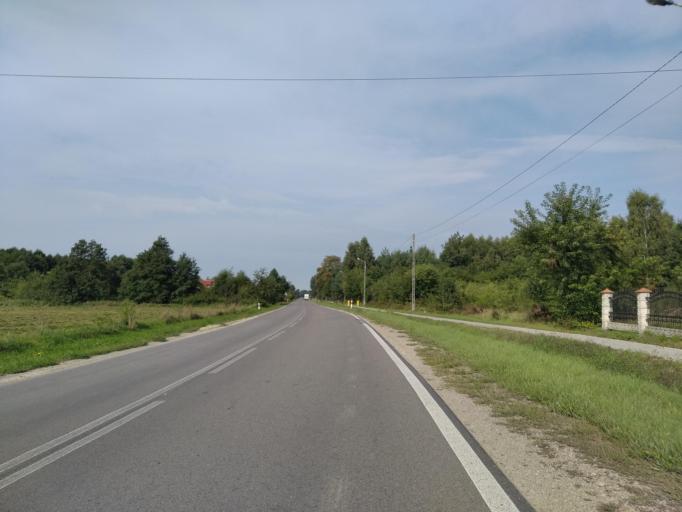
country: PL
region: Subcarpathian Voivodeship
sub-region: Powiat mielecki
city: Przeclaw
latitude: 50.1613
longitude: 21.5307
